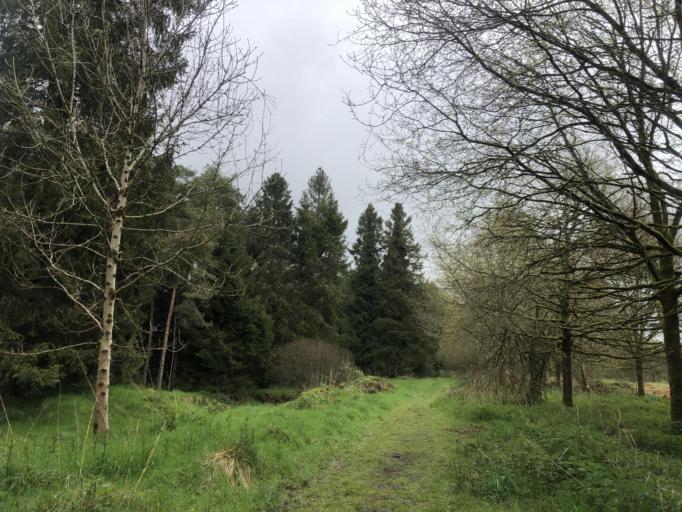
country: IE
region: Connaught
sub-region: County Leitrim
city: Carrick-on-Shannon
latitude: 53.9842
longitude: -8.1835
